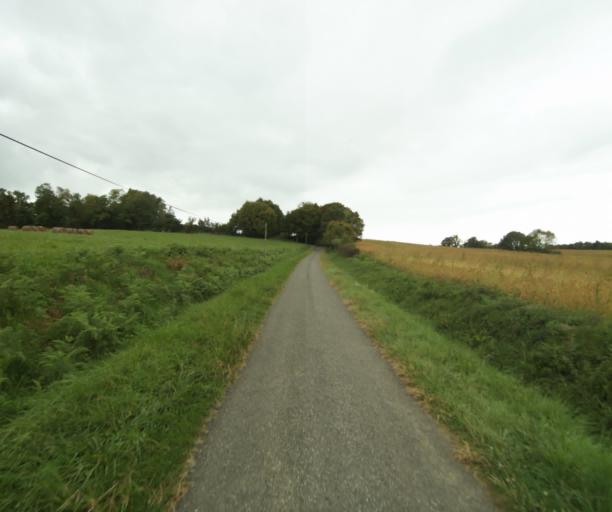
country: FR
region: Midi-Pyrenees
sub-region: Departement du Gers
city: Eauze
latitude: 43.8977
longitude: 0.0552
